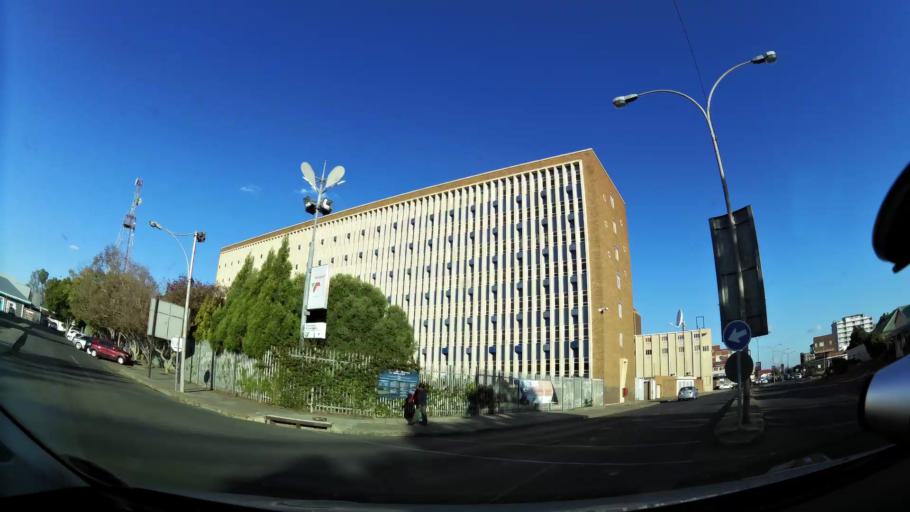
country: ZA
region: Northern Cape
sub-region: Frances Baard District Municipality
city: Kimberley
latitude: -28.7359
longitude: 24.7686
